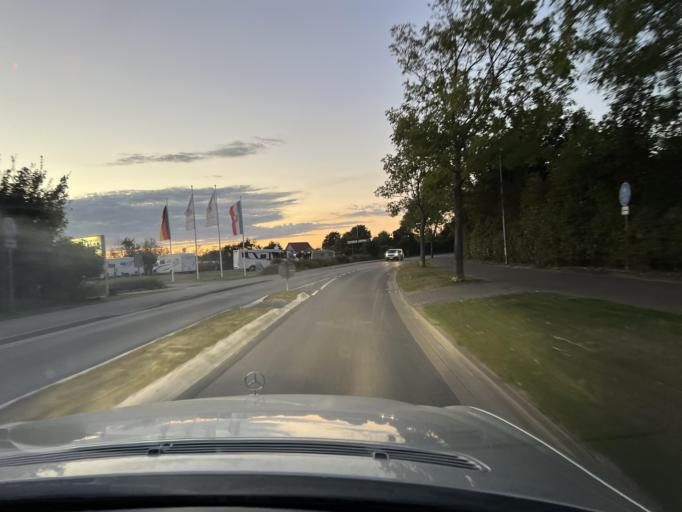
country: DE
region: Schleswig-Holstein
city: Busum
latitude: 54.1385
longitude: 8.8437
